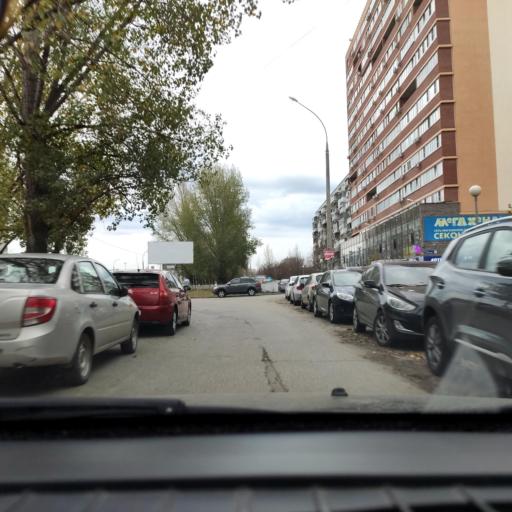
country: RU
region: Samara
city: Tol'yatti
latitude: 53.5347
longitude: 49.3434
